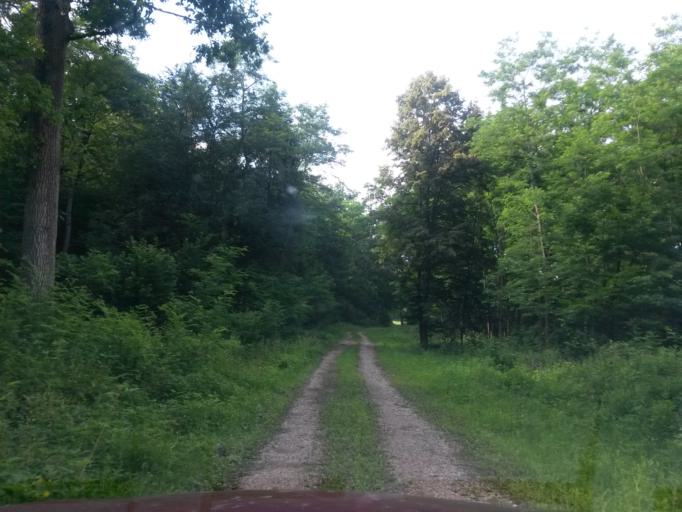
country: SK
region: Kosicky
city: Moldava nad Bodvou
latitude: 48.6136
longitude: 21.1126
